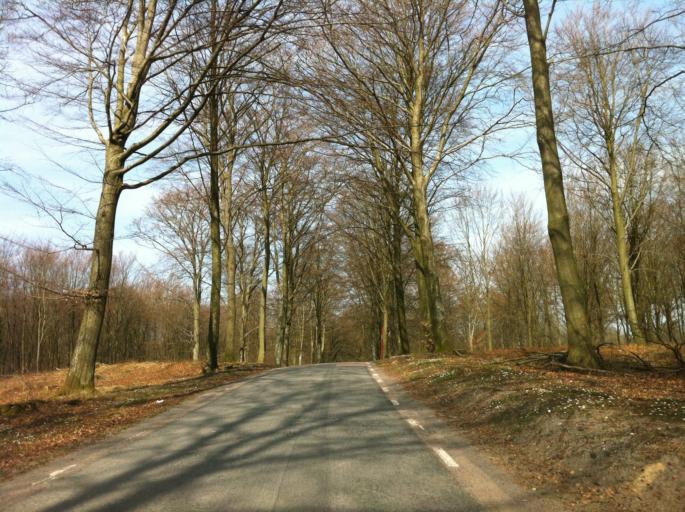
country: SE
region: Skane
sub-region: Klippans Kommun
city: Ljungbyhed
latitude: 55.9838
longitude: 13.1990
